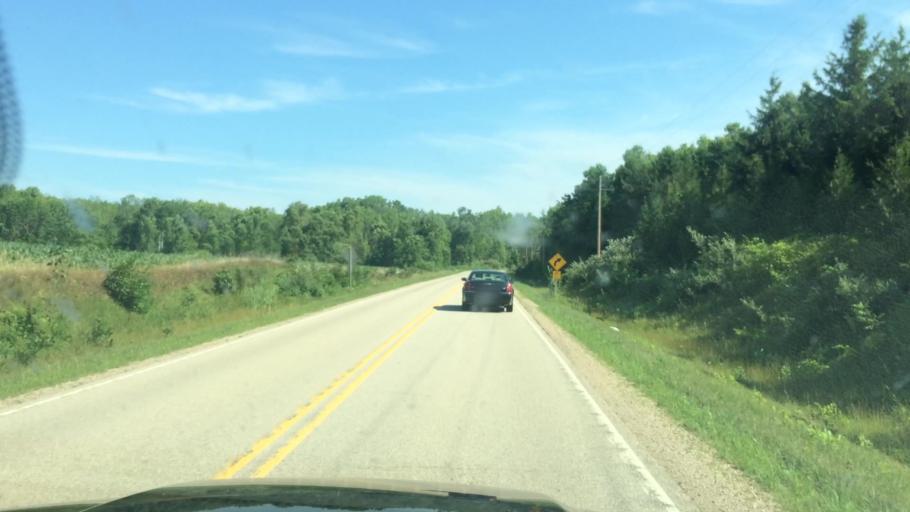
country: US
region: Wisconsin
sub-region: Oconto County
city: Gillett
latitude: 44.7908
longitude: -88.3119
